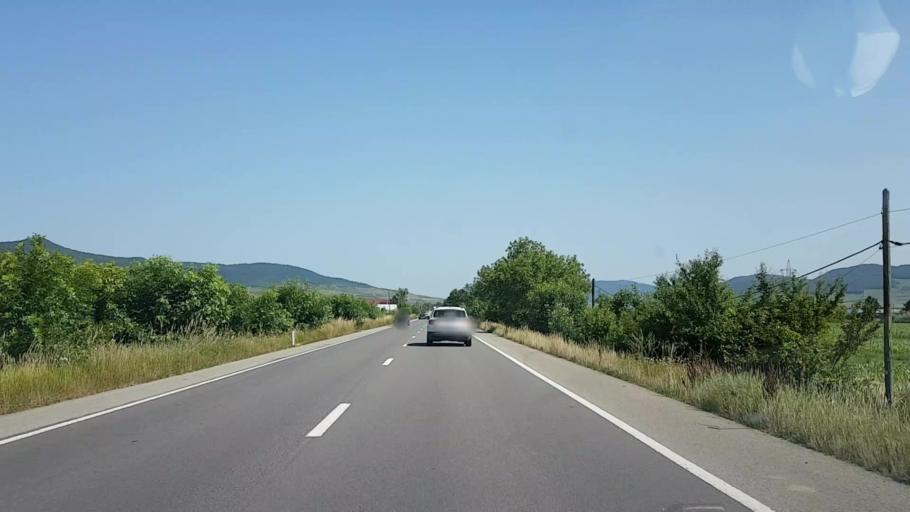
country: RO
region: Bistrita-Nasaud
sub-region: Comuna Sieu-Magherus
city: Sieu-Magherus
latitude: 47.1029
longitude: 24.3569
